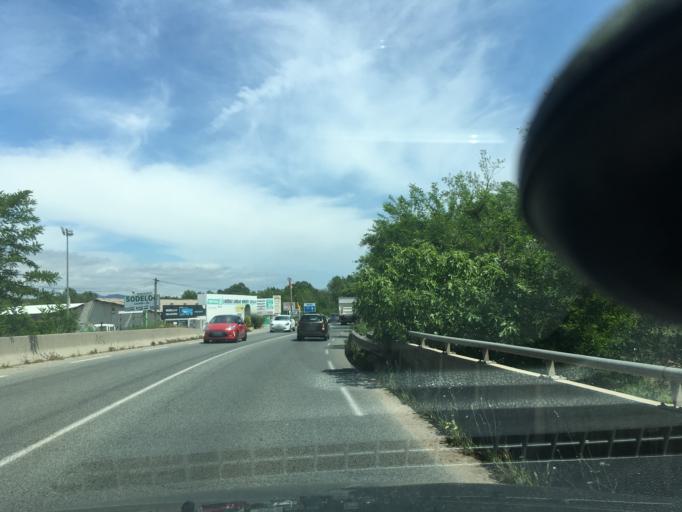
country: FR
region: Provence-Alpes-Cote d'Azur
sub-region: Departement du Var
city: Roquebrune-sur-Argens
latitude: 43.4623
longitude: 6.6480
